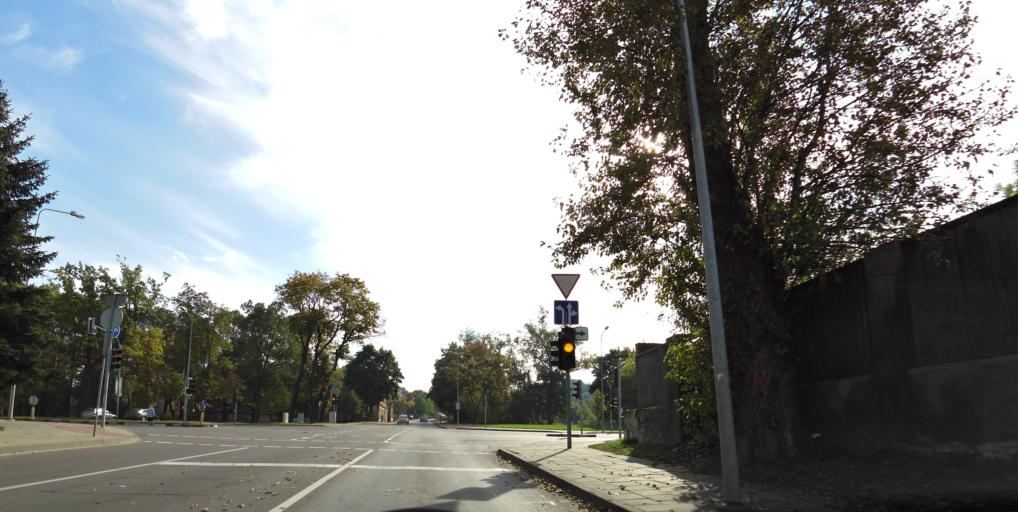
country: LT
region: Vilnius County
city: Rasos
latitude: 54.6740
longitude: 25.2979
